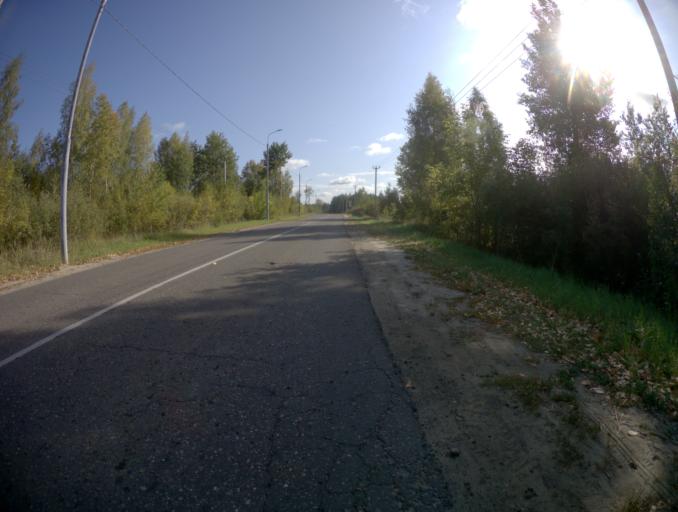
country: RU
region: Moskovskaya
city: Roshal'
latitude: 55.6719
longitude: 39.8546
